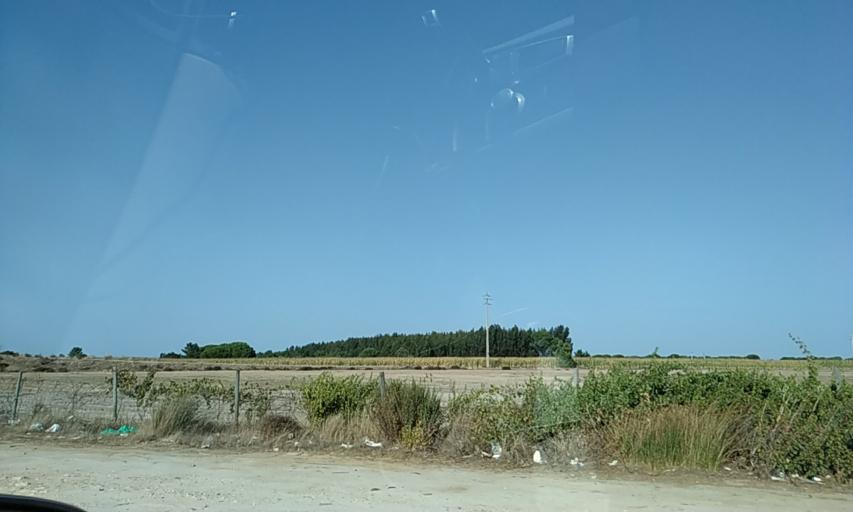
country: PT
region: Santarem
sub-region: Almeirim
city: Almeirim
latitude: 39.1714
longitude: -8.6206
